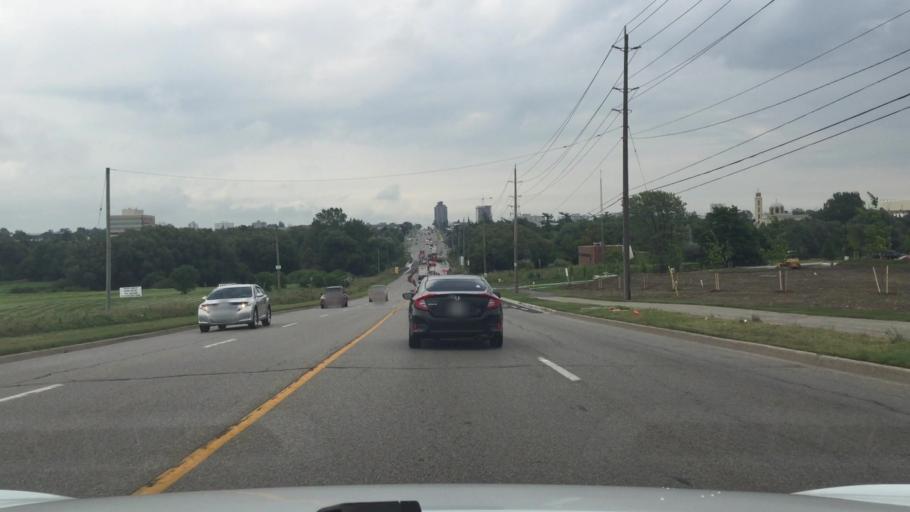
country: CA
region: Ontario
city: Ajax
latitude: 43.8381
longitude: -79.0448
